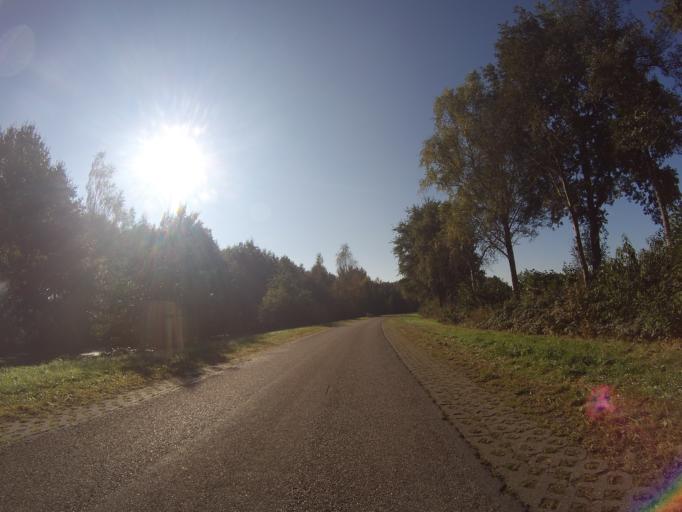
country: NL
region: Drenthe
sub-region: Gemeente Coevorden
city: Sleen
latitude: 52.7416
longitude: 6.7898
